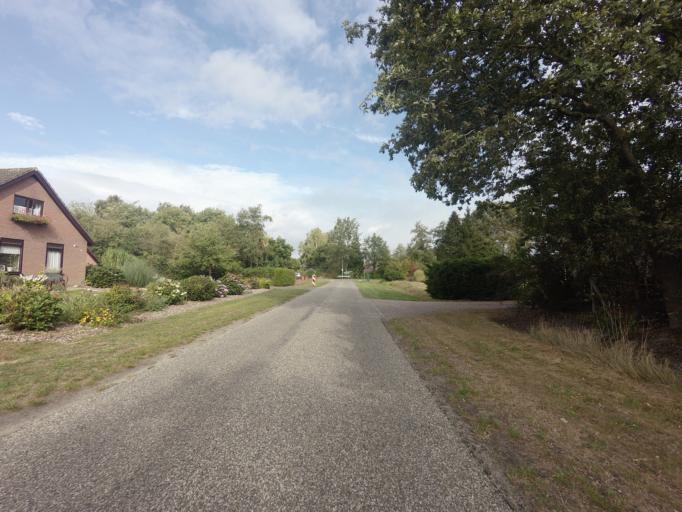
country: NL
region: Friesland
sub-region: Gemeente Heerenveen
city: Jubbega
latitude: 52.9860
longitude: 6.1148
